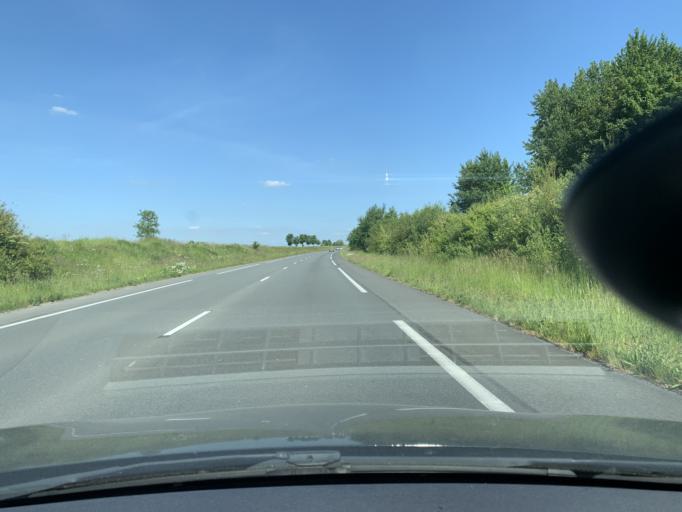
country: FR
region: Nord-Pas-de-Calais
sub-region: Departement du Nord
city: Cambrai
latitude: 50.1518
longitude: 3.2531
